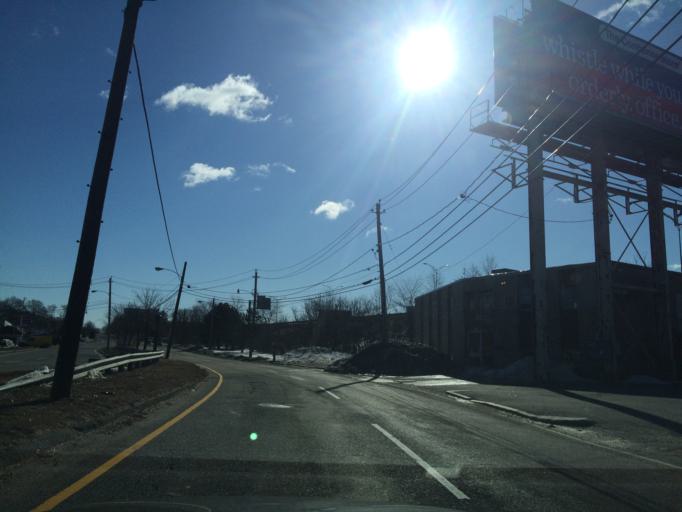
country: US
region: Massachusetts
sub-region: Middlesex County
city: Watertown
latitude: 42.3584
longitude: -71.1578
